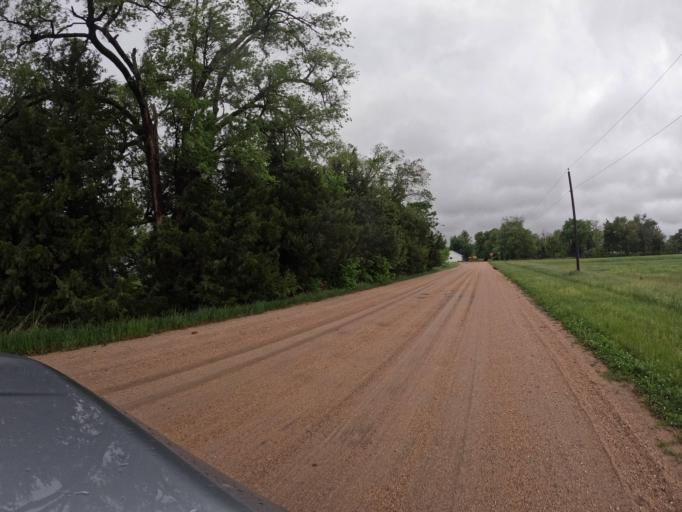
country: US
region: Nebraska
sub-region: Clay County
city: Harvard
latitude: 40.6268
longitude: -98.0992
